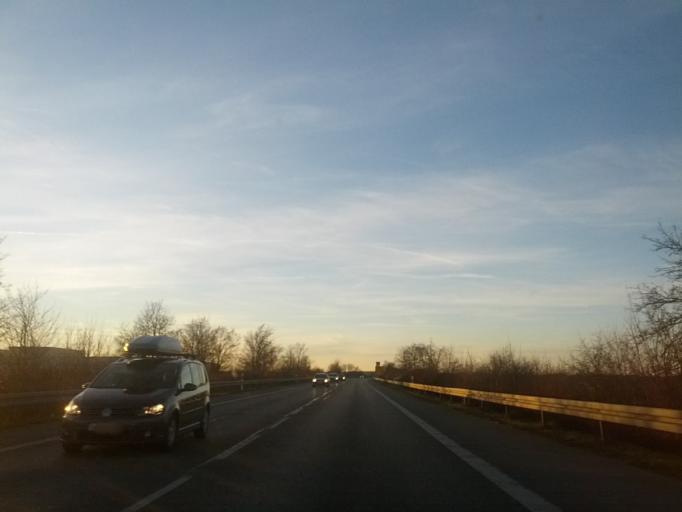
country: DE
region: Bavaria
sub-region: Swabia
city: Heimertingen
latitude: 48.0352
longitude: 10.1267
